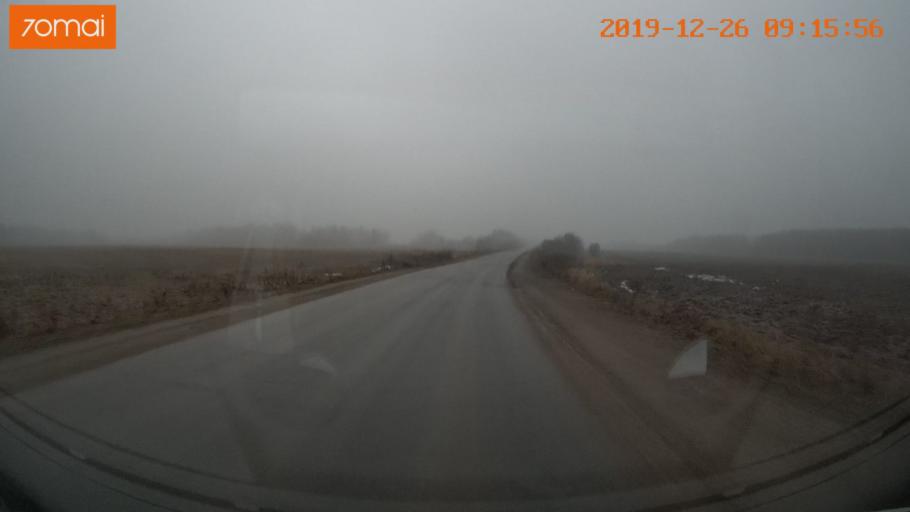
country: RU
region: Vologda
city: Gryazovets
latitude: 58.9114
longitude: 40.2388
